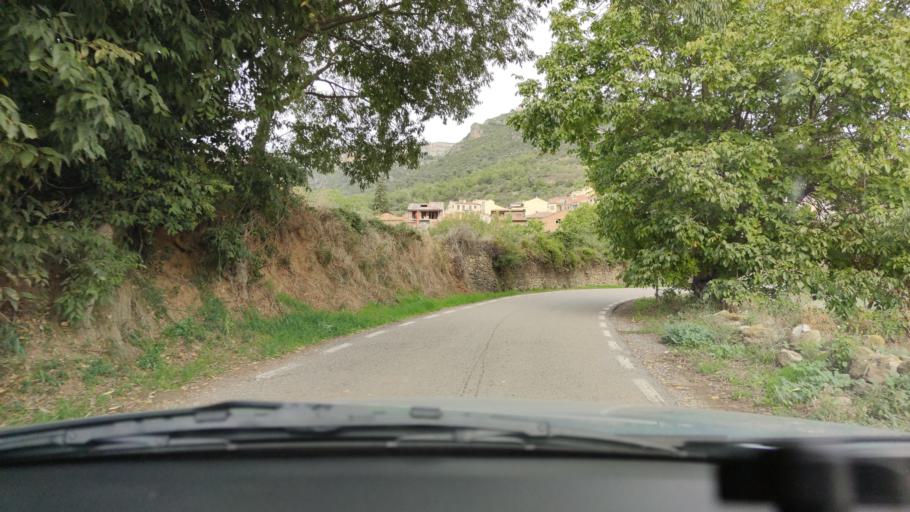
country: ES
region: Catalonia
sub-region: Provincia de Lleida
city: Artesa de Segre
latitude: 41.9927
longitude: 1.0228
